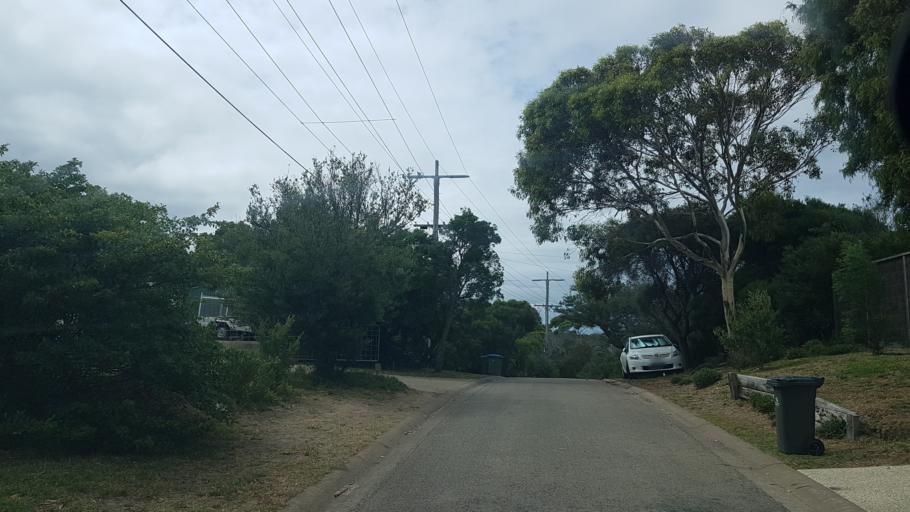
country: AU
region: Victoria
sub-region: Mornington Peninsula
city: Blairgowrie
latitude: -38.3678
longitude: 144.7733
